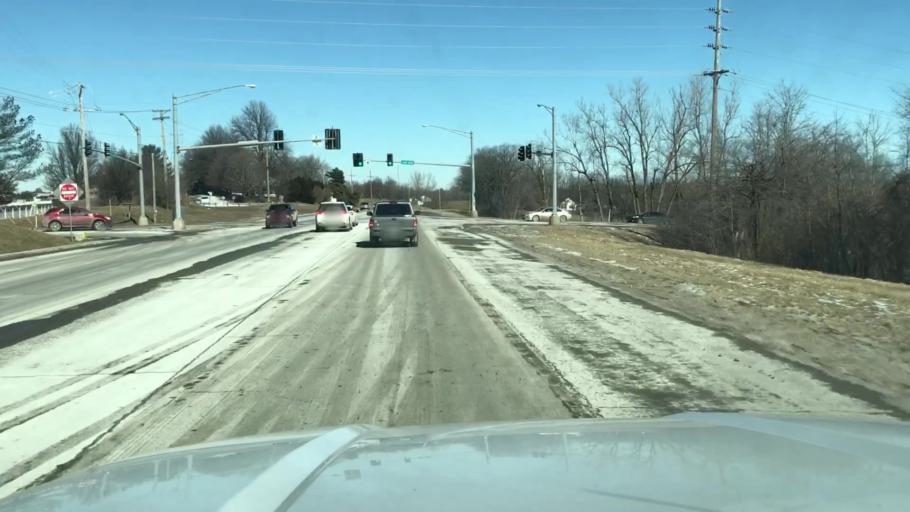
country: US
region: Missouri
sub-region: Andrew County
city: Country Club Village
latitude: 39.8061
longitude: -94.8106
